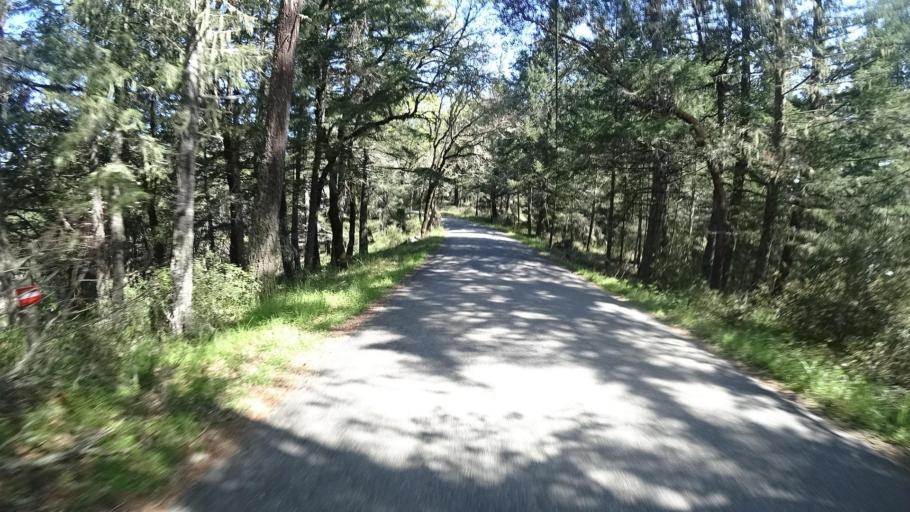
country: US
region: California
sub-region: Humboldt County
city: Redway
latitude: 40.0462
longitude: -123.6423
